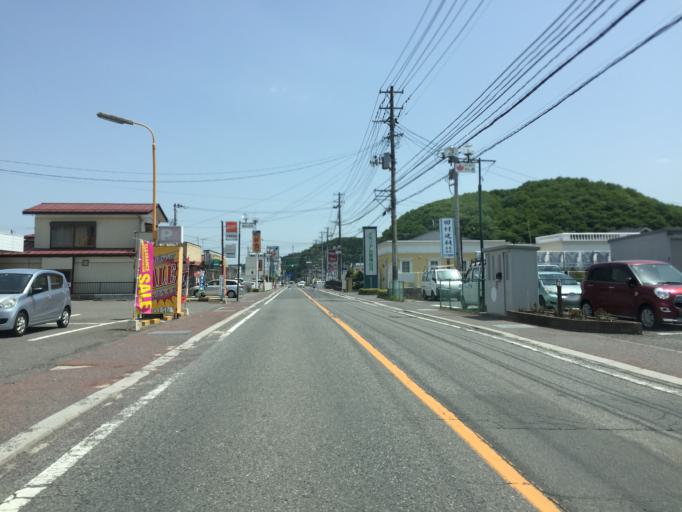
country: JP
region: Fukushima
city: Ishikawa
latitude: 37.1199
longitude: 140.2295
